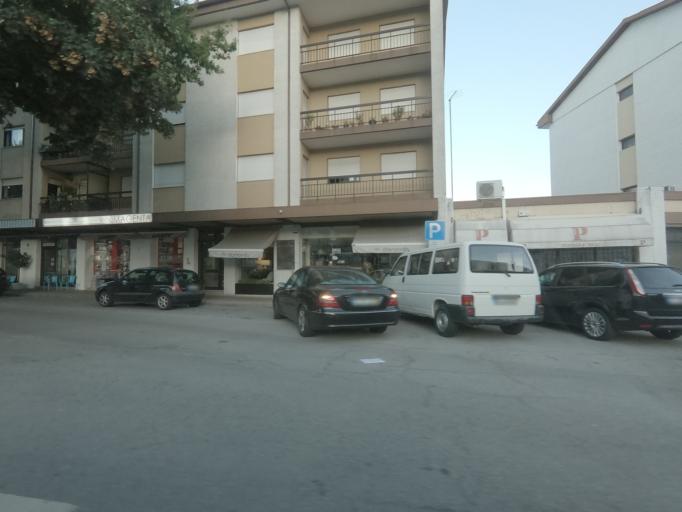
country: PT
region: Vila Real
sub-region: Vila Real
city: Vila Real
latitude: 41.3065
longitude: -7.7415
